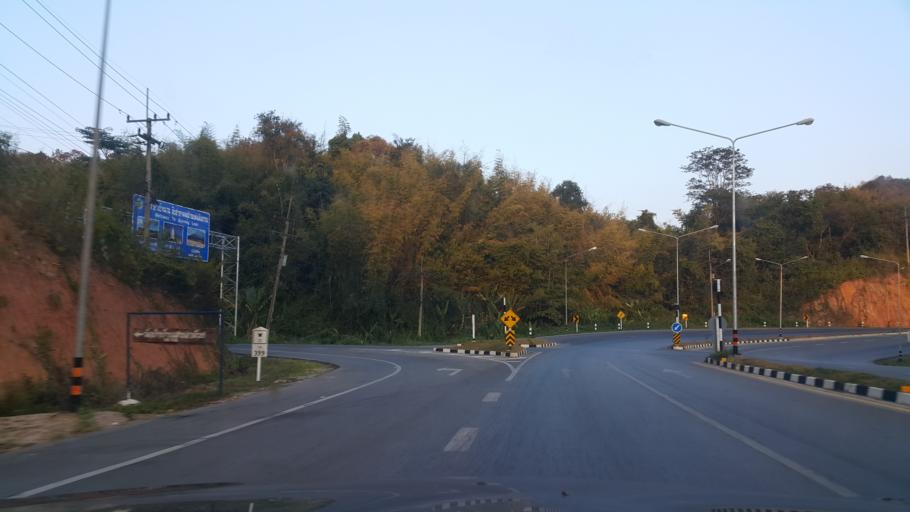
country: TH
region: Loei
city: Loei
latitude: 17.4822
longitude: 101.6193
